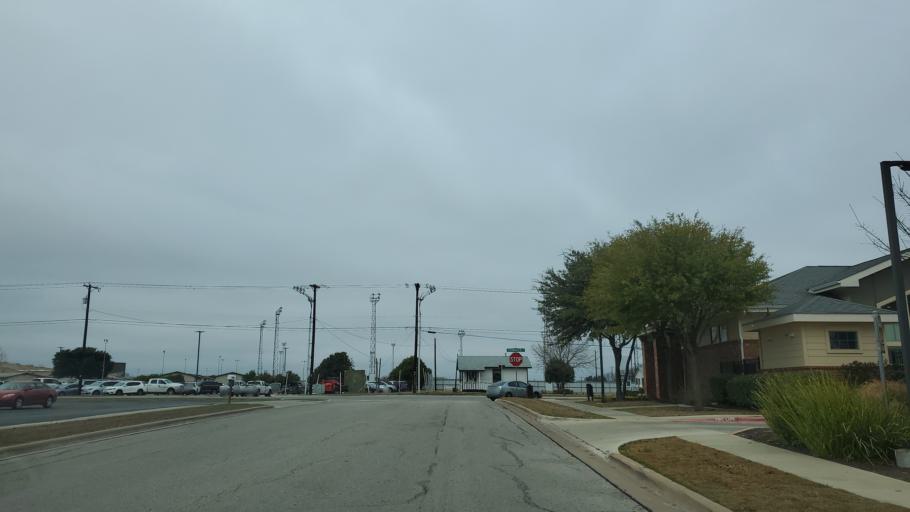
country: US
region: Texas
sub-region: Bell County
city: Killeen
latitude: 31.0847
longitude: -97.7356
